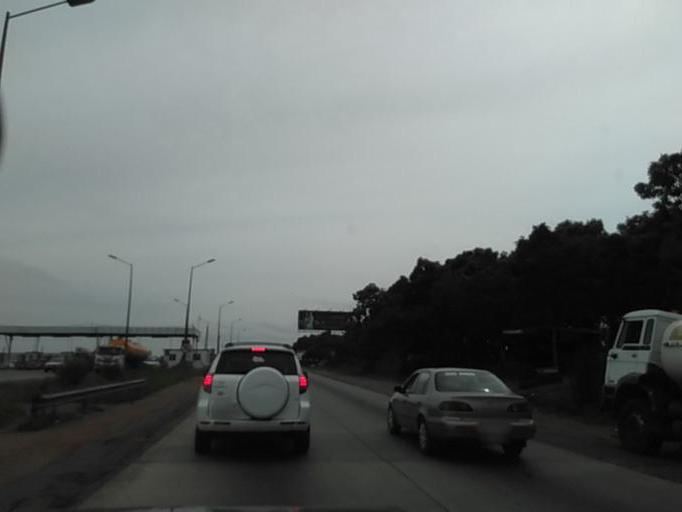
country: GH
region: Greater Accra
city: Medina Estates
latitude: 5.6348
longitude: -0.1438
